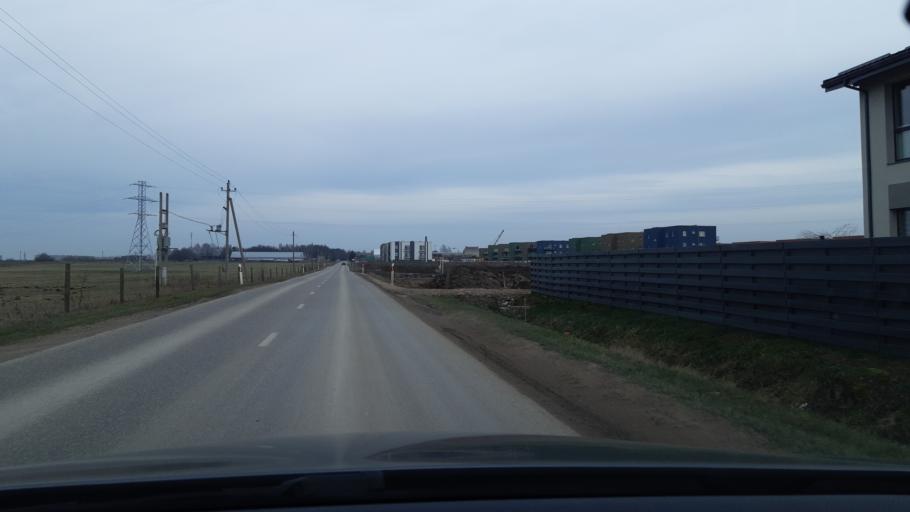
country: LT
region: Kauno apskritis
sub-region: Kaunas
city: Sargenai
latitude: 54.9522
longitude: 23.8507
